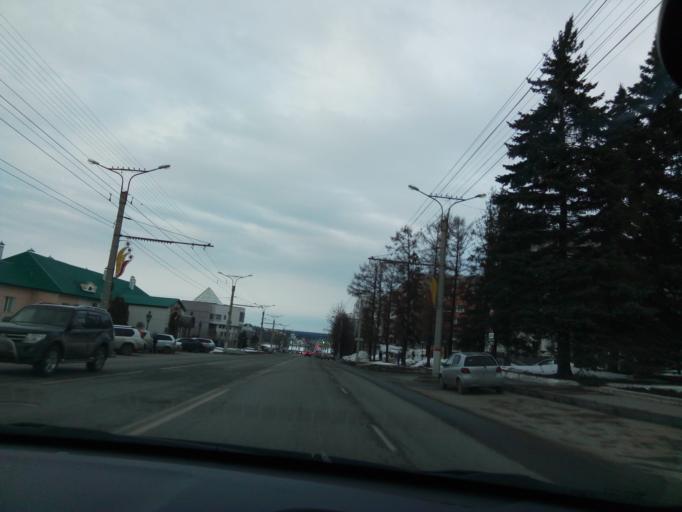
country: RU
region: Chuvashia
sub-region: Cheboksarskiy Rayon
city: Cheboksary
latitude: 56.1404
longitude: 47.2443
